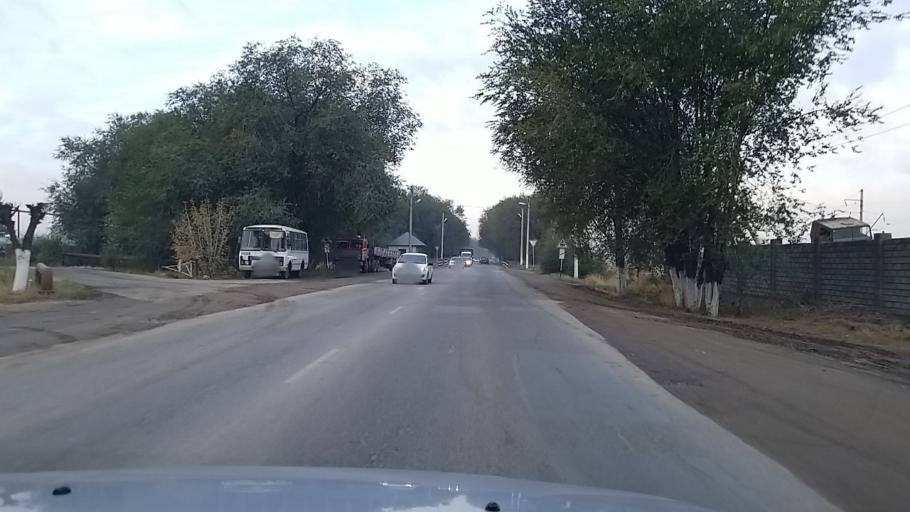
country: KZ
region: Almaty Oblysy
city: Burunday
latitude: 43.3557
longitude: 76.7998
